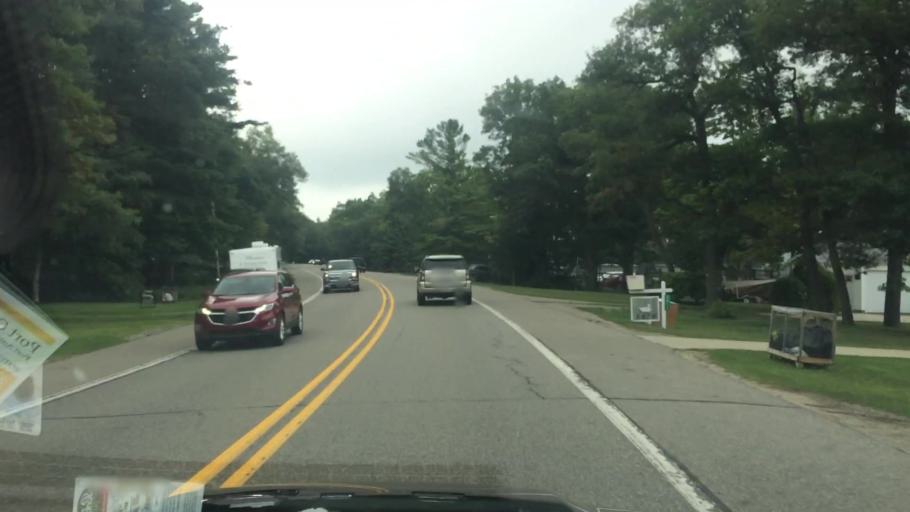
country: US
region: Michigan
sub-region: Huron County
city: Pigeon
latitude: 43.9718
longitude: -83.2599
